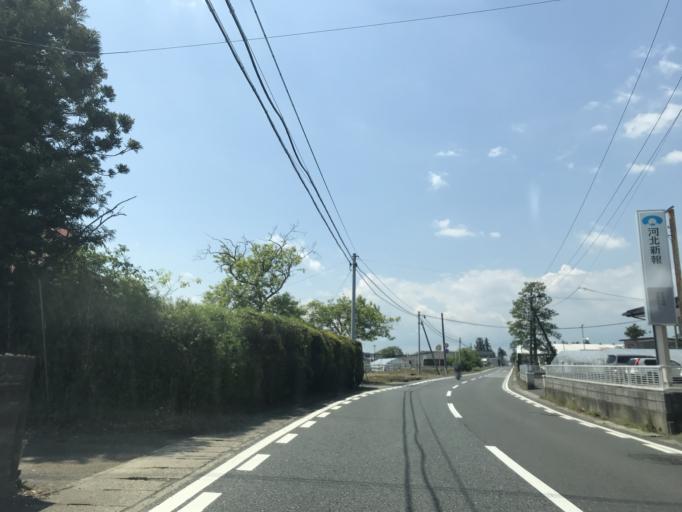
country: JP
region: Miyagi
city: Kogota
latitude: 38.5858
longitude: 141.0365
